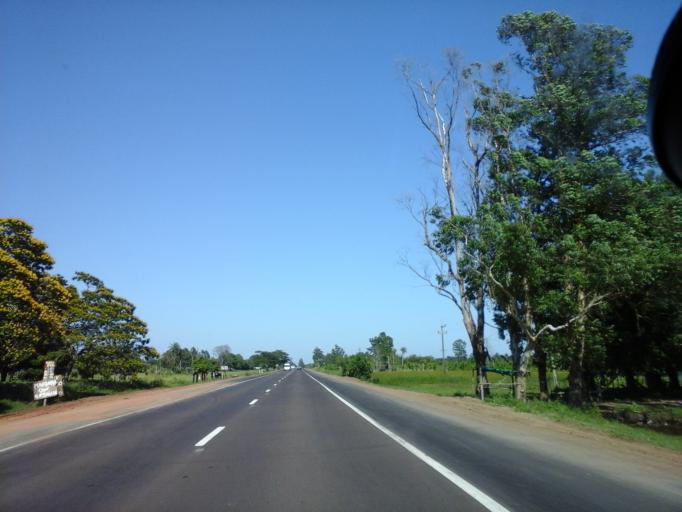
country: AR
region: Corrientes
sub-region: Departamento de Itati
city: Itati
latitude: -27.3670
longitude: -58.3454
